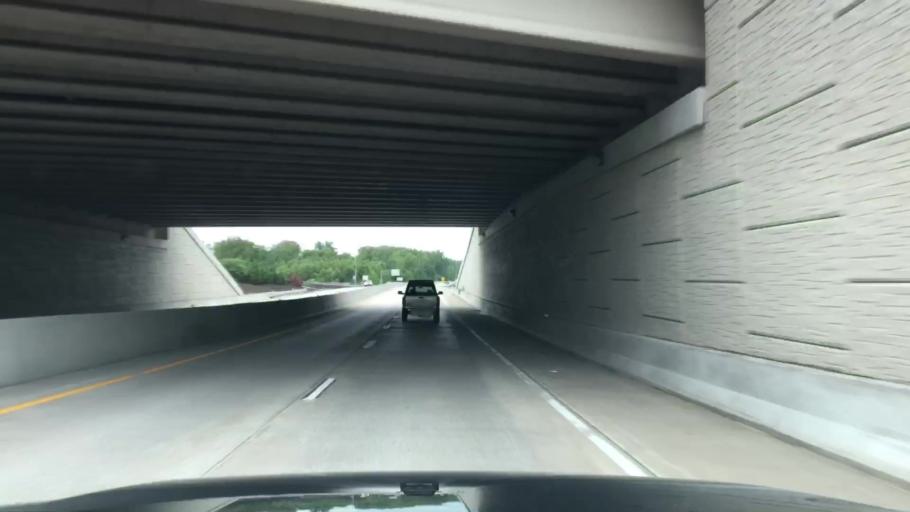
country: US
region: Missouri
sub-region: Saint Louis County
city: Maryland Heights
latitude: 38.6815
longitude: -90.4934
